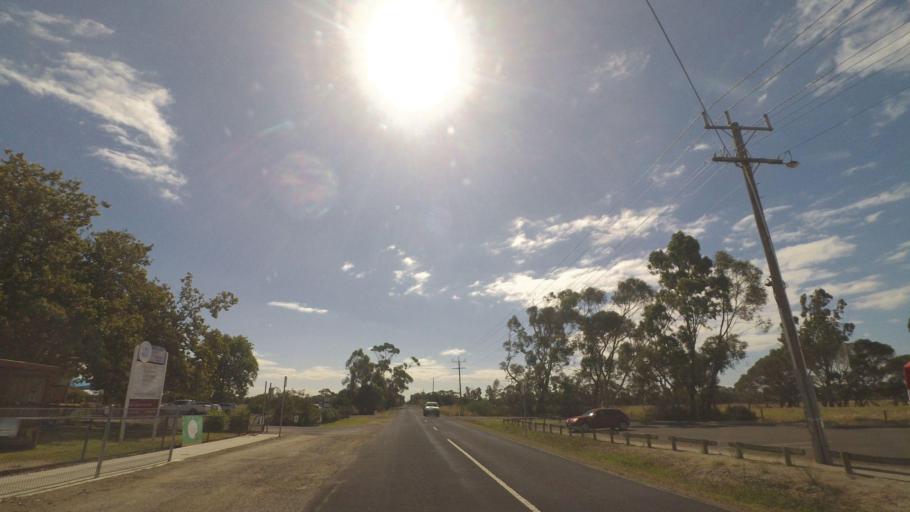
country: AU
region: Victoria
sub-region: Cardinia
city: Pakenham South
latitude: -38.1760
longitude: 145.5666
